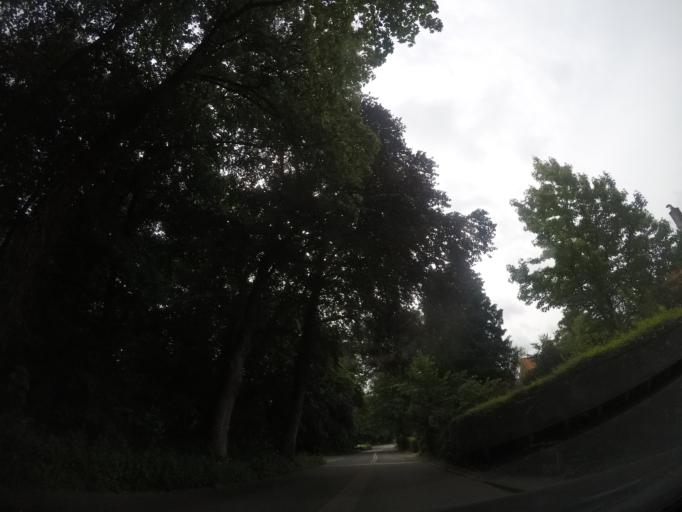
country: NL
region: Gelderland
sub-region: Gemeente Arnhem
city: Gulden Bodem
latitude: 51.9944
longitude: 5.8946
